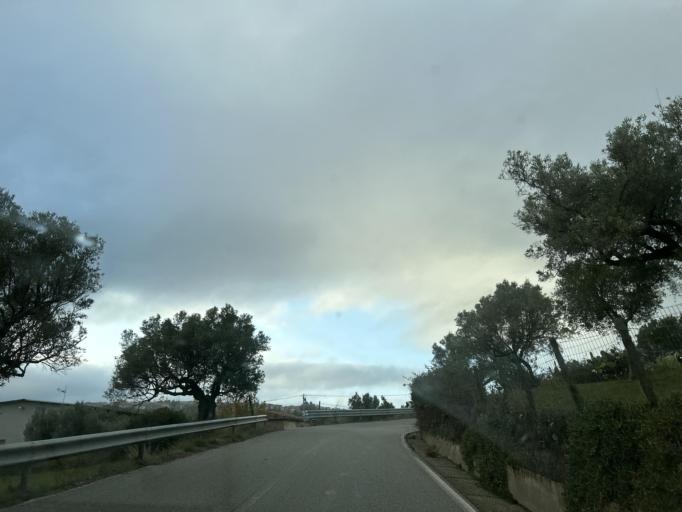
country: IT
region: Calabria
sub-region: Provincia di Catanzaro
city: Staletti
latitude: 38.7618
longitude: 16.5567
